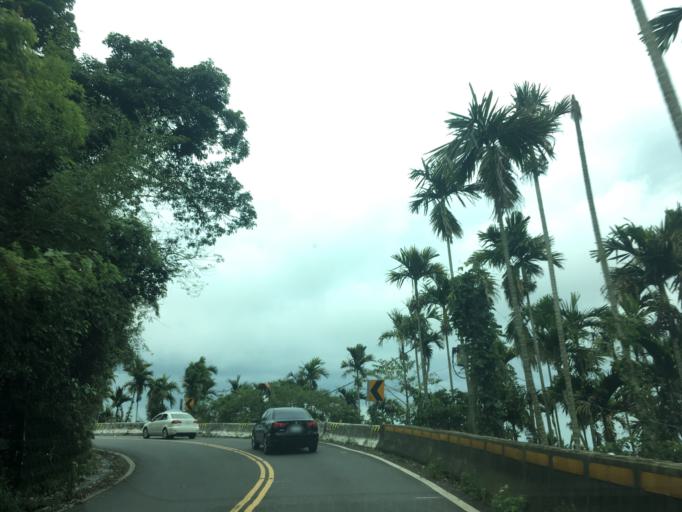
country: TW
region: Taiwan
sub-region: Yunlin
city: Douliu
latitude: 23.5630
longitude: 120.5905
